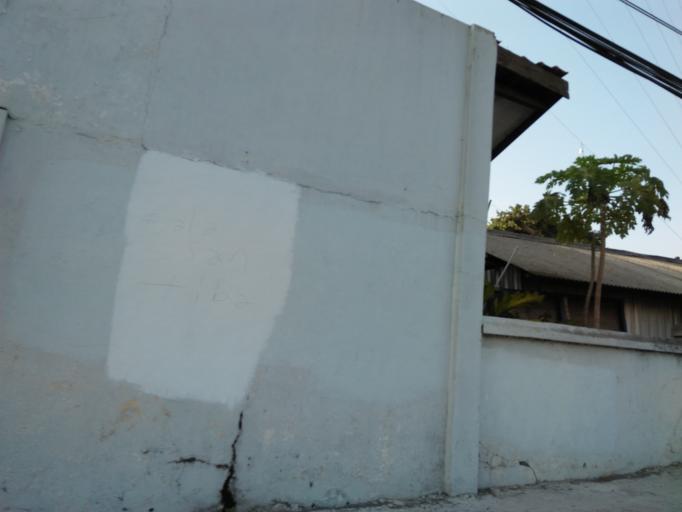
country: ID
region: Daerah Istimewa Yogyakarta
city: Depok
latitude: -7.7741
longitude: 110.4643
